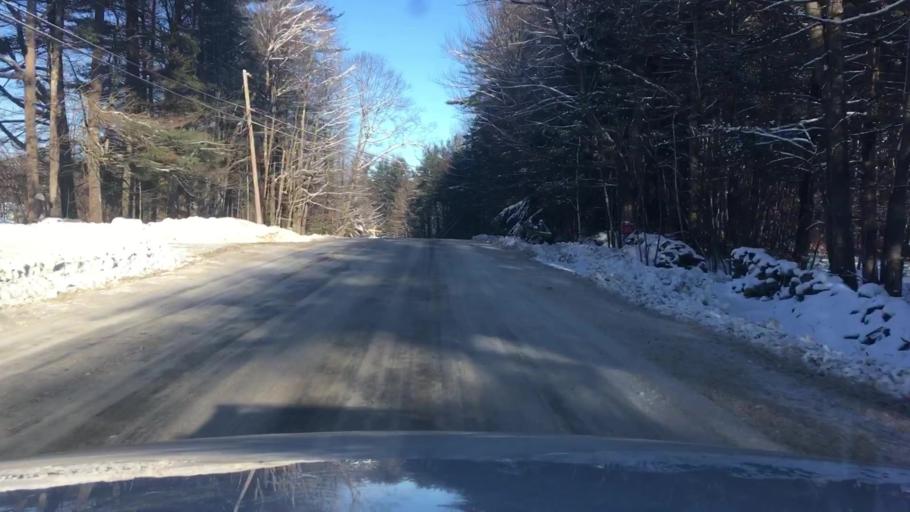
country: US
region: Maine
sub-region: Kennebec County
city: Readfield
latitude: 44.4171
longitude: -69.9217
